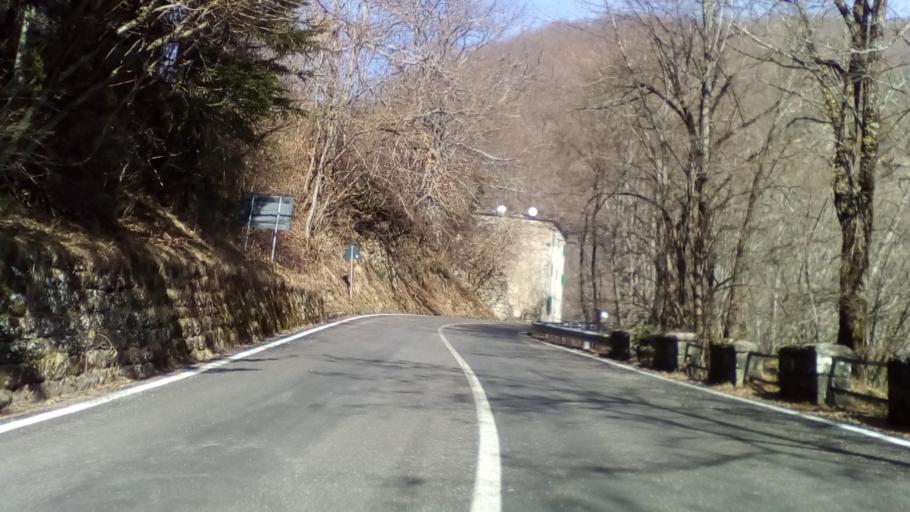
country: IT
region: Emilia-Romagna
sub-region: Provincia di Modena
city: Pievepelago
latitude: 44.2167
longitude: 10.6145
